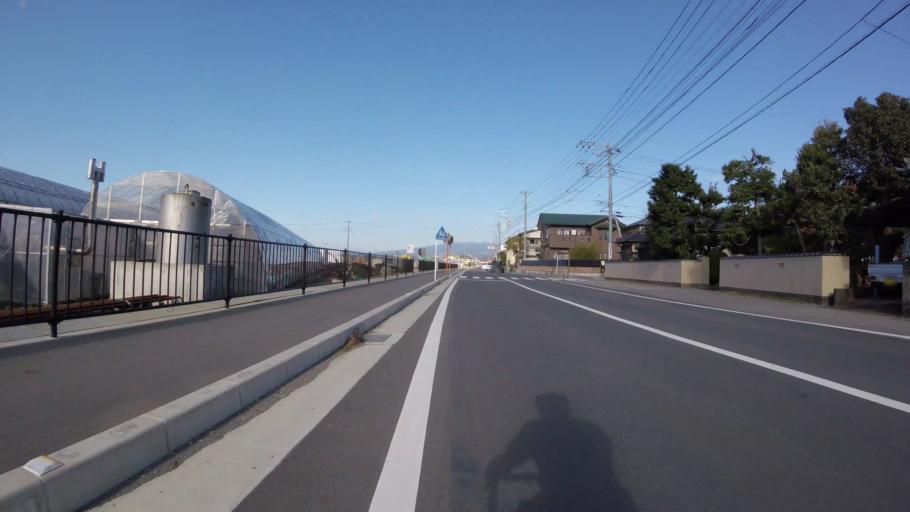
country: JP
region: Shizuoka
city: Mishima
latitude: 35.0523
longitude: 138.9527
